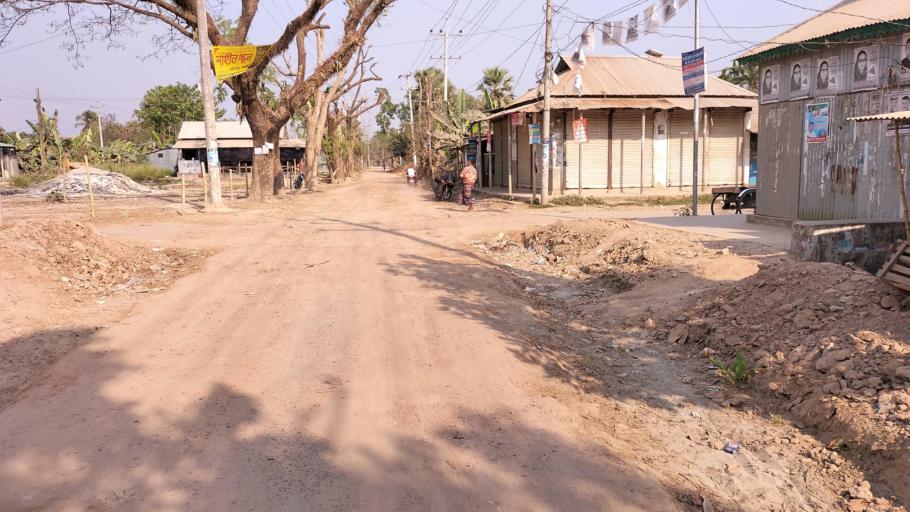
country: BD
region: Dhaka
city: Sakhipur
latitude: 24.3074
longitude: 90.3076
